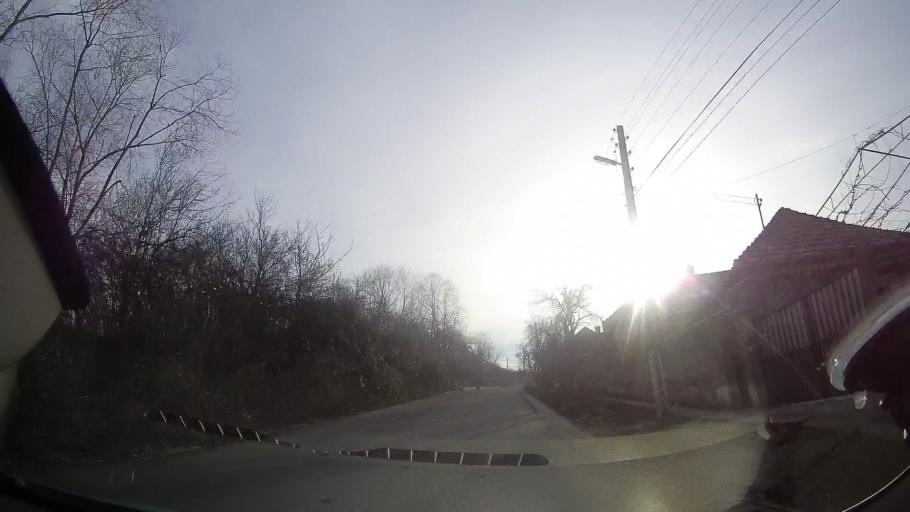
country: RO
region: Bihor
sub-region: Comuna Sarbi
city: Burzuc
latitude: 47.1446
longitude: 22.1859
